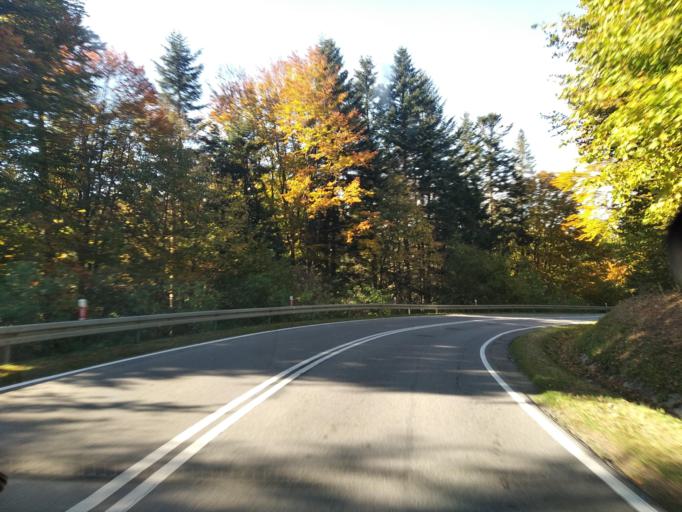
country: PL
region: Subcarpathian Voivodeship
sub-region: Powiat leski
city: Cisna
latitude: 49.2453
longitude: 22.2899
